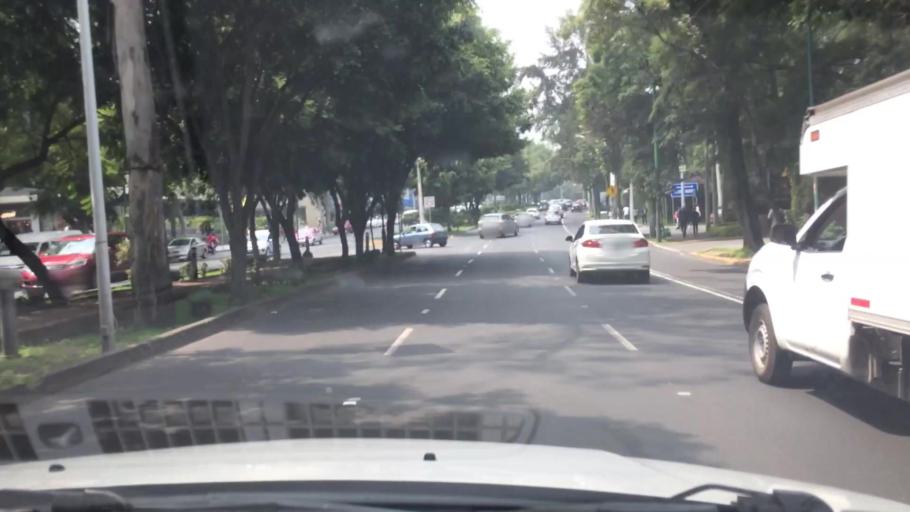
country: MX
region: Mexico City
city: Coyoacan
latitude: 19.3465
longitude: -99.1782
